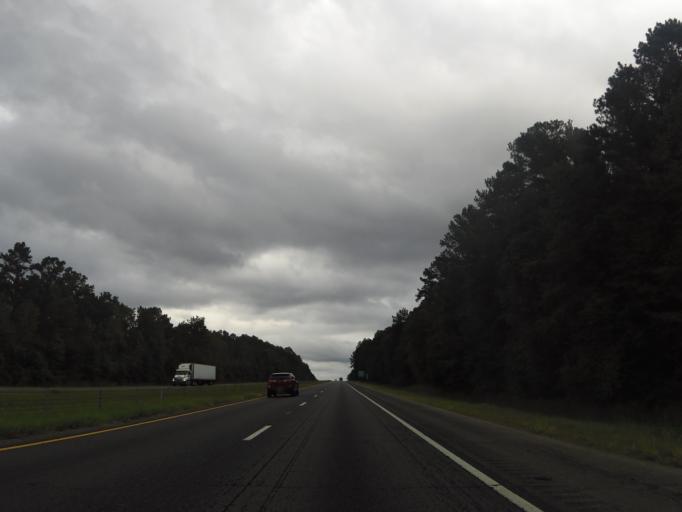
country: US
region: Alabama
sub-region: Butler County
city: Georgiana
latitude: 31.5619
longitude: -86.8630
